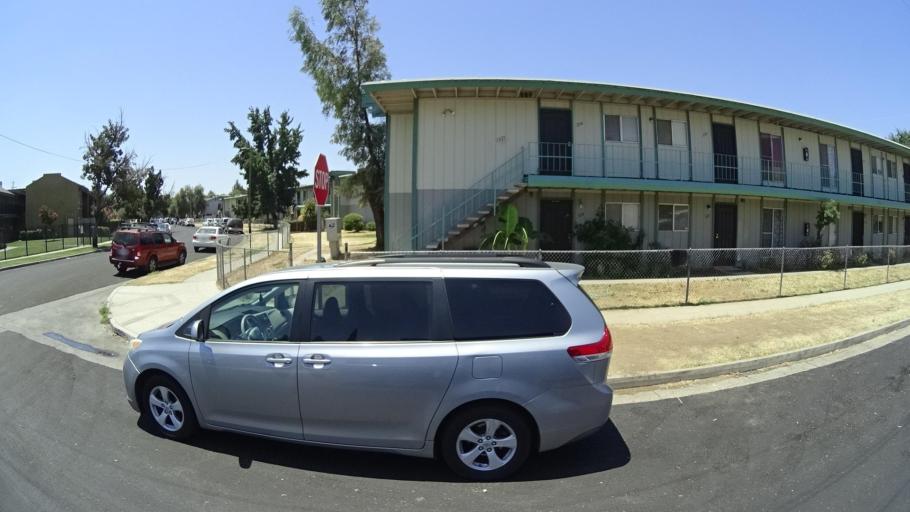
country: US
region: California
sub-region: Fresno County
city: Sunnyside
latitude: 36.7594
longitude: -119.7207
